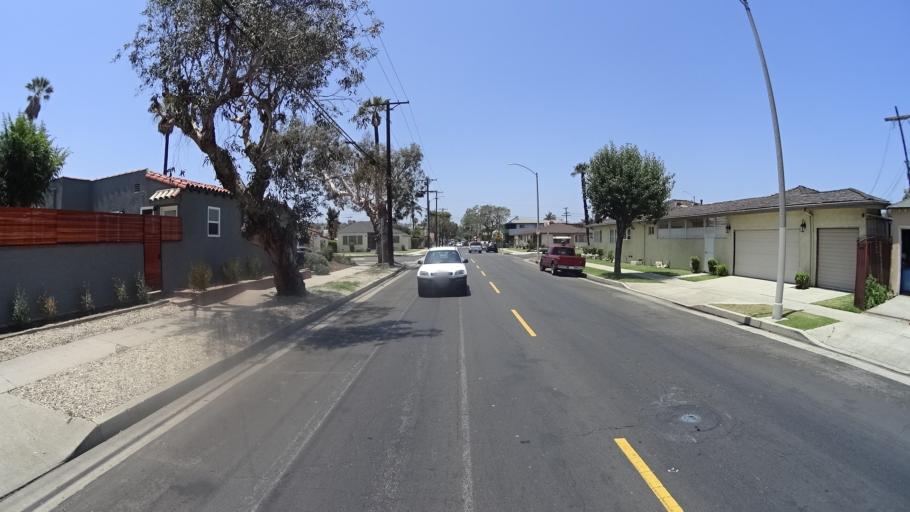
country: US
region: California
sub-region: Los Angeles County
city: View Park-Windsor Hills
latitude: 34.0146
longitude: -118.3323
